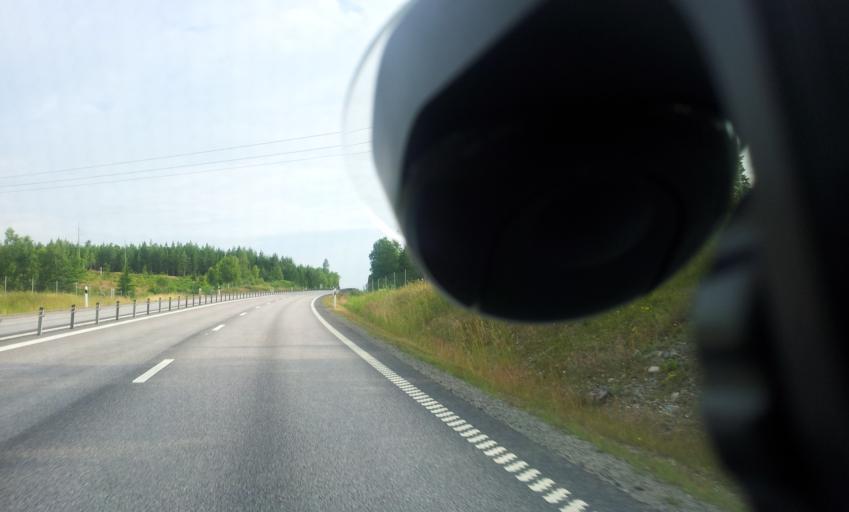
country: SE
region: OEstergoetland
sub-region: Valdemarsviks Kommun
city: Gusum
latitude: 58.2907
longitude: 16.4964
